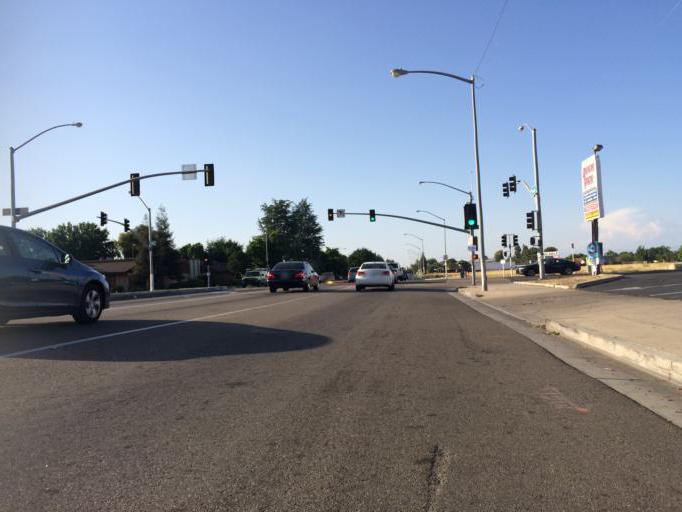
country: US
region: California
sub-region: Fresno County
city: Sunnyside
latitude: 36.7571
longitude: -119.7182
